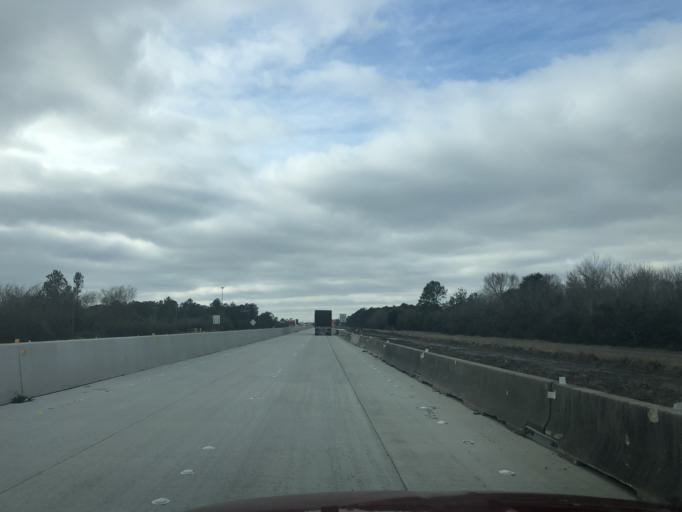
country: US
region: Texas
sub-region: Chambers County
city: Winnie
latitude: 29.8506
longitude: -94.3662
